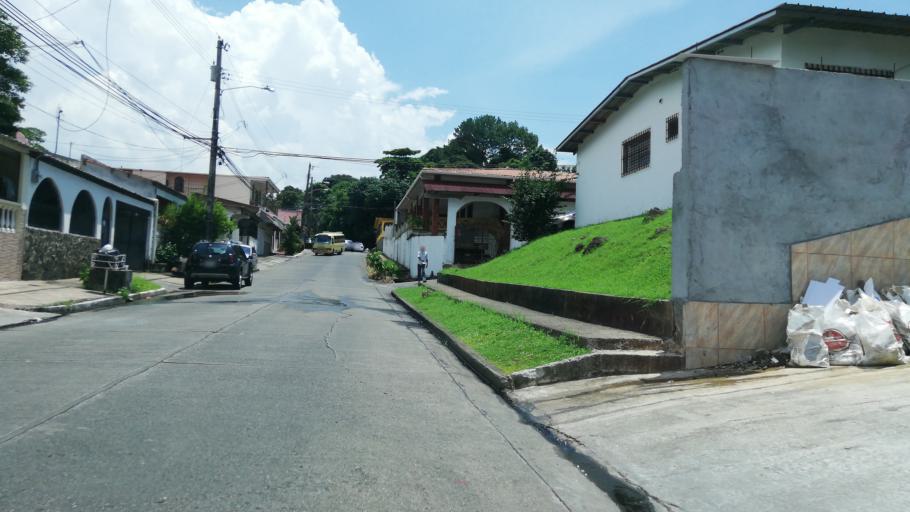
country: PA
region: Panama
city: San Miguelito
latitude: 9.0619
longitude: -79.4533
